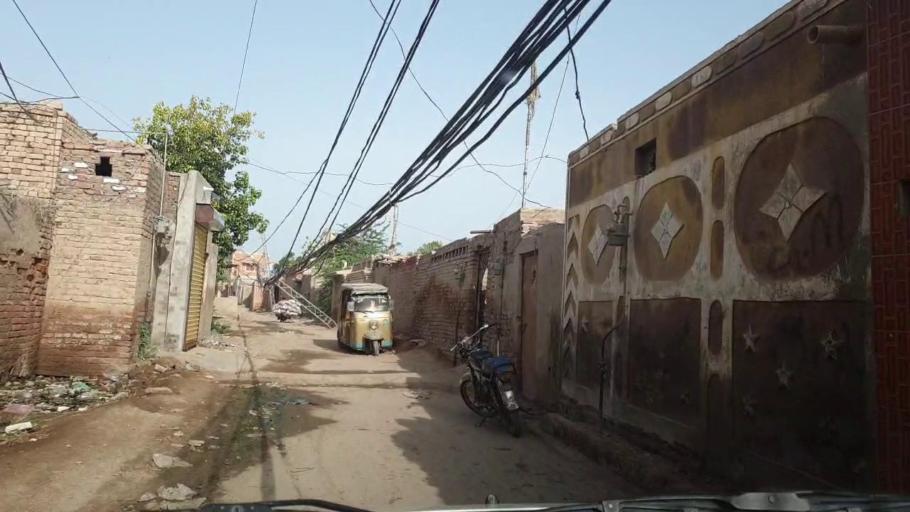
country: PK
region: Sindh
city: Nawabshah
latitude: 26.2337
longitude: 68.4033
